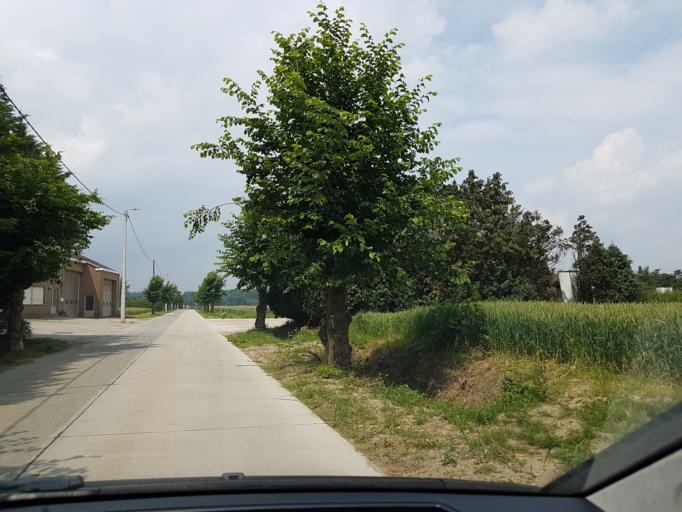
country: BE
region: Flanders
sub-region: Provincie Vlaams-Brabant
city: Steenokkerzeel
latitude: 50.9385
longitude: 4.5088
